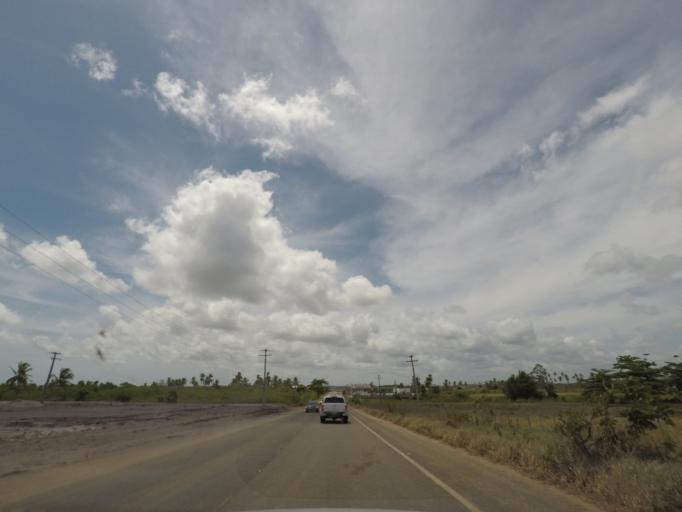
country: BR
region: Sergipe
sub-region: Indiaroba
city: Indiaroba
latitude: -11.5137
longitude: -37.5104
